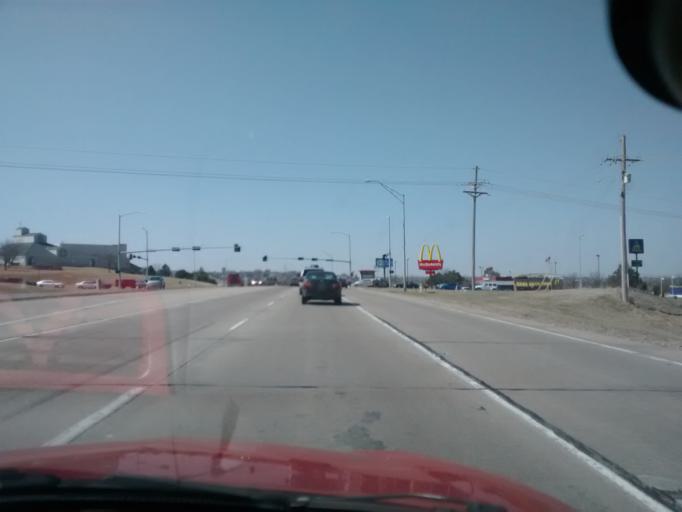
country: US
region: Nebraska
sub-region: Sarpy County
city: Offutt Air Force Base
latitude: 41.1391
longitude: -95.9659
